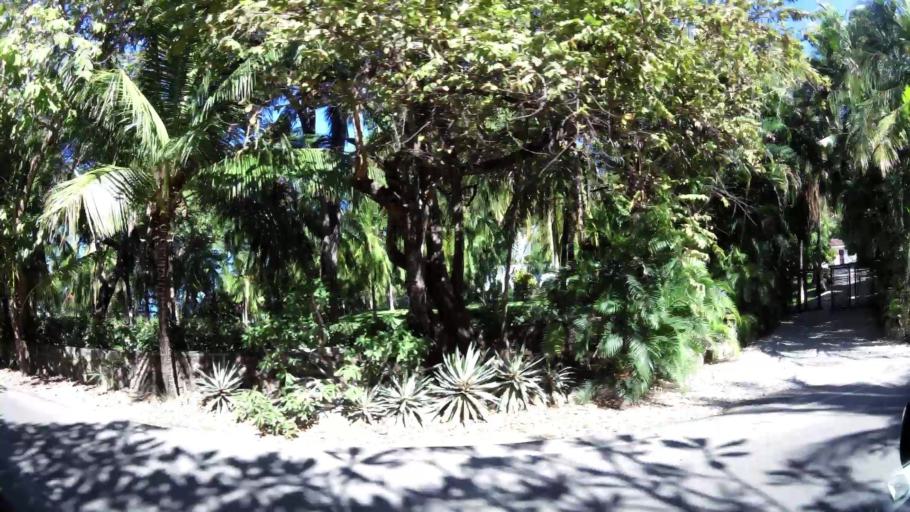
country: CR
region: Guanacaste
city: Sardinal
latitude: 10.4393
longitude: -85.7927
